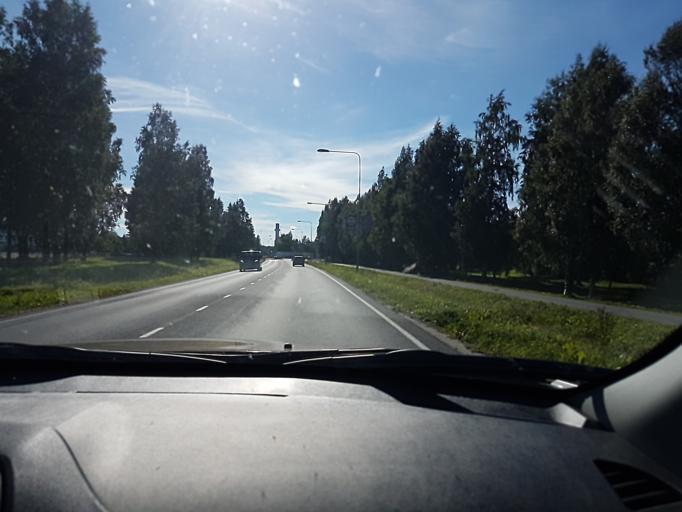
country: FI
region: Southern Ostrobothnia
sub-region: Seinaejoki
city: Seinaejoki
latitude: 62.7910
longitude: 22.8641
